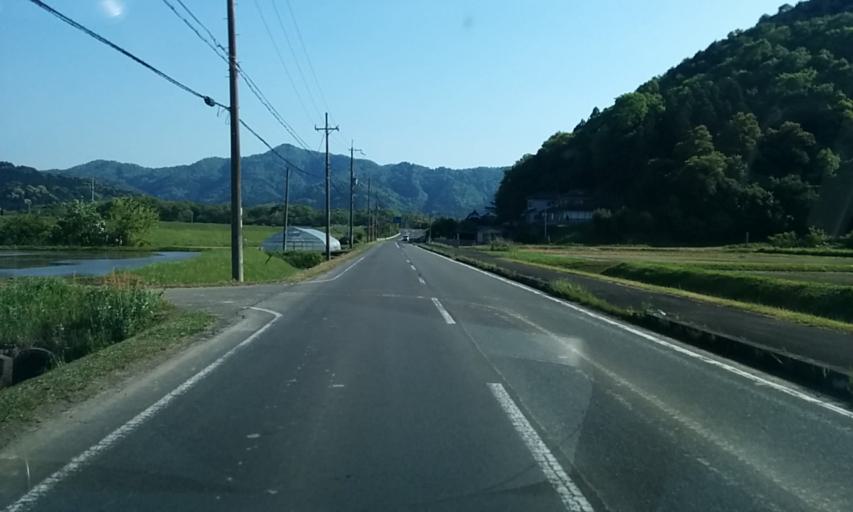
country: JP
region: Kyoto
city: Ayabe
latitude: 35.3143
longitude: 135.2088
